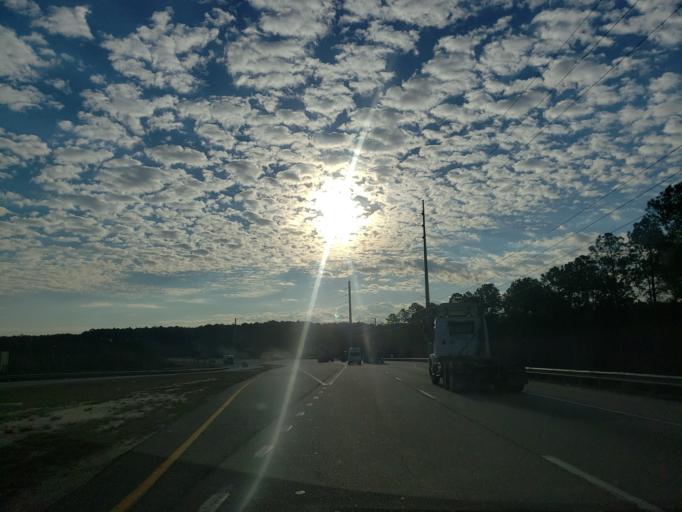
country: US
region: Georgia
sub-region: Chatham County
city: Port Wentworth
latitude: 32.1646
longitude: -81.2135
